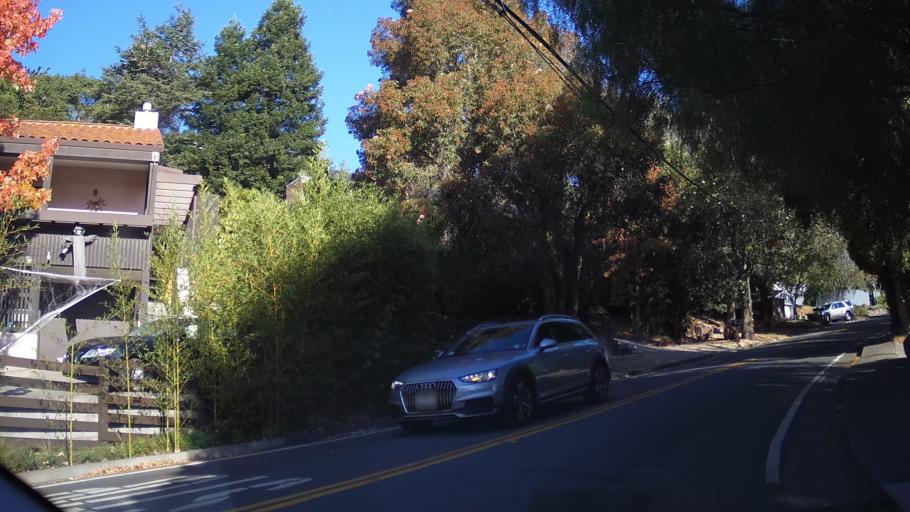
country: US
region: California
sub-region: Marin County
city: Mill Valley
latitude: 37.8971
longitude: -122.5402
